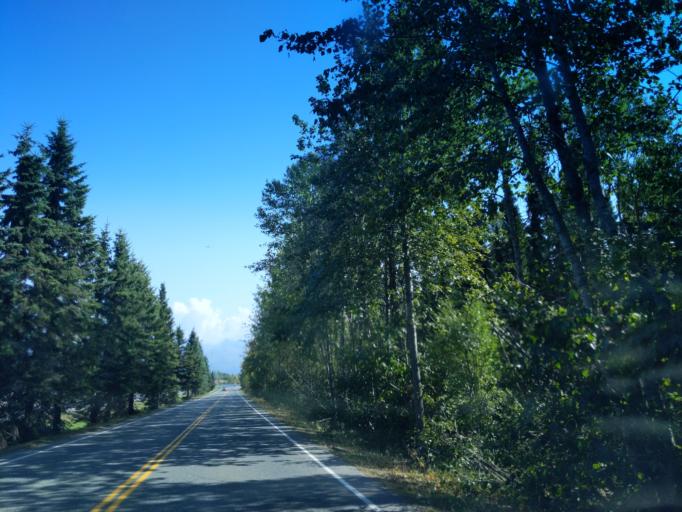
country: US
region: Alaska
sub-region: Anchorage Municipality
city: Anchorage
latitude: 61.1728
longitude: -149.9332
